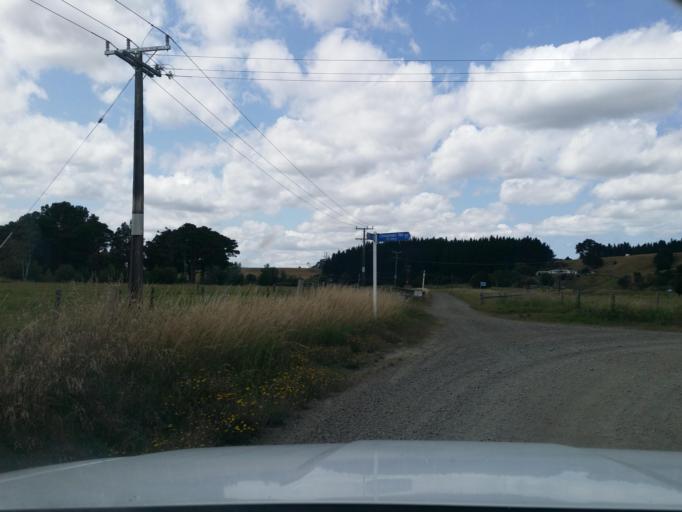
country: NZ
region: Northland
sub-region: Kaipara District
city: Dargaville
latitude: -35.8088
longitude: 173.7310
